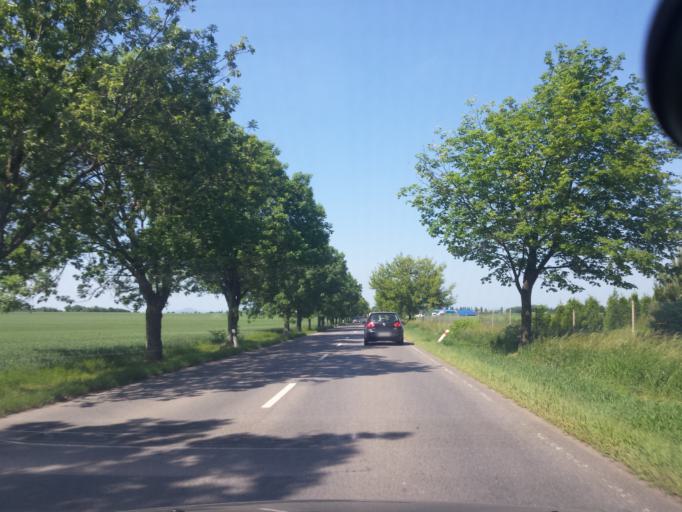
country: CZ
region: Central Bohemia
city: Velke Prilepy
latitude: 50.1738
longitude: 14.3180
